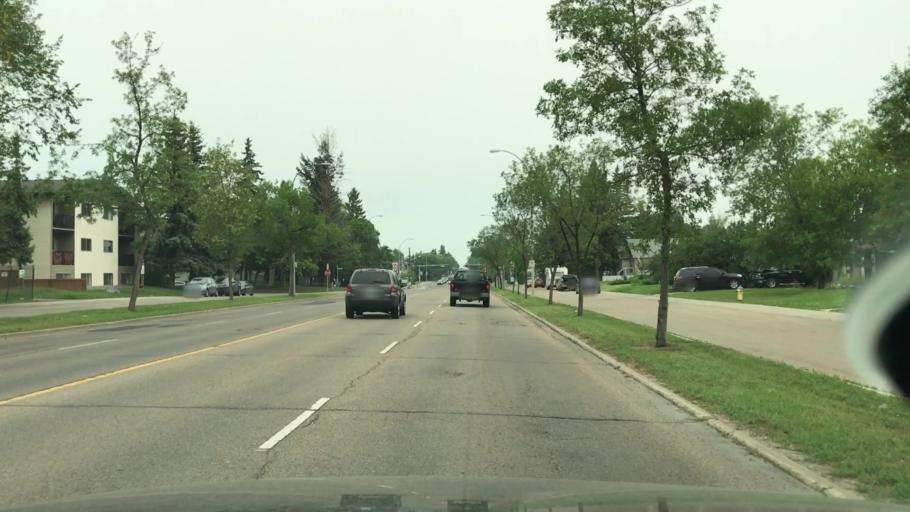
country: CA
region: Alberta
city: Edmonton
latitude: 53.5291
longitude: -113.5779
